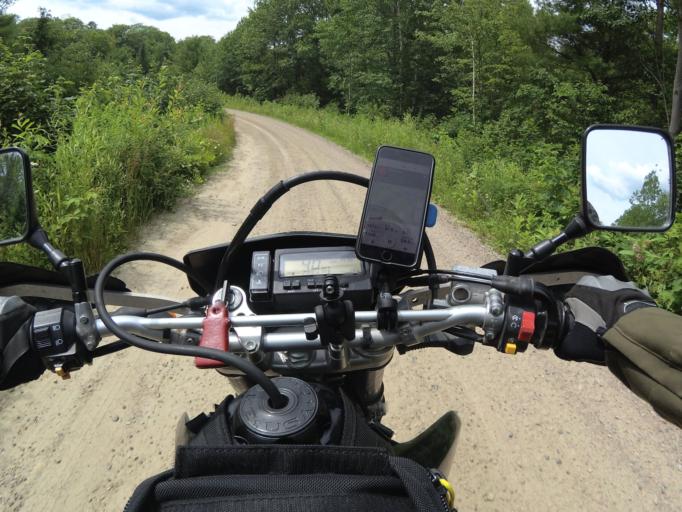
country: CA
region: Ontario
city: Bancroft
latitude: 44.8278
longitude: -77.3068
